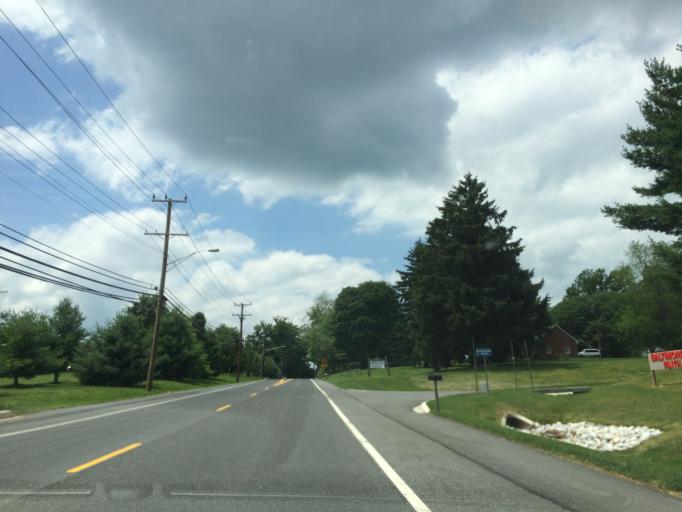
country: US
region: Maryland
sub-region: Baltimore County
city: Randallstown
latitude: 39.3882
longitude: -76.8366
